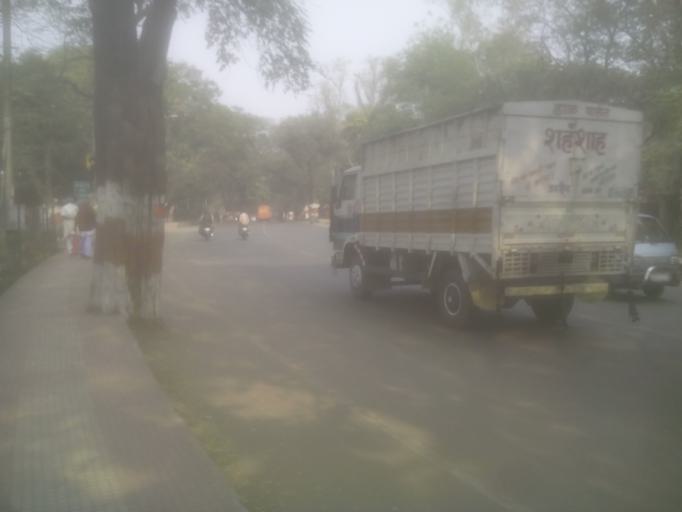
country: IN
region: Jharkhand
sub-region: Dhanbad
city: Dhanbad
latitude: 23.8030
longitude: 86.4273
